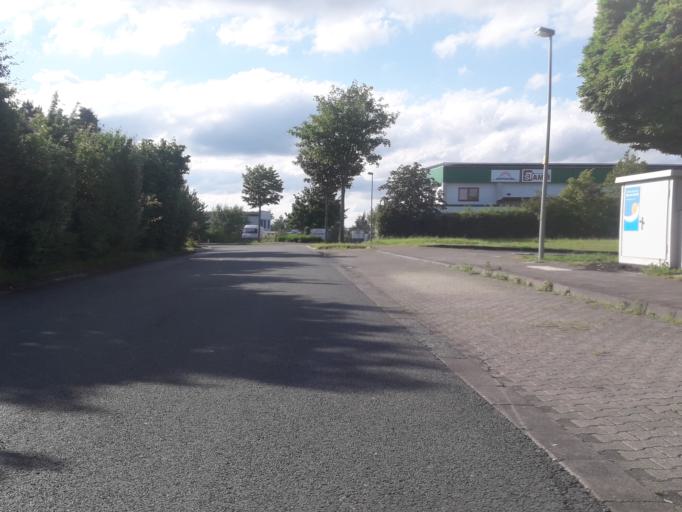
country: DE
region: North Rhine-Westphalia
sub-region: Regierungsbezirk Detmold
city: Paderborn
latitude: 51.7262
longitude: 8.7984
